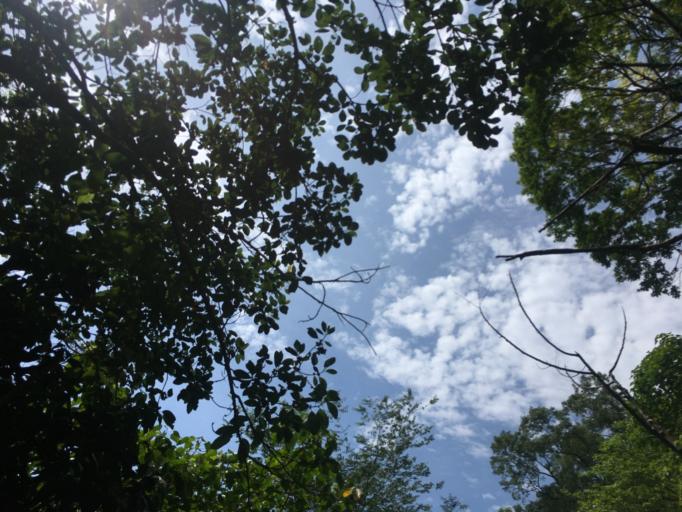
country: TW
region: Taiwan
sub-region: Hualien
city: Hualian
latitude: 24.0200
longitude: 121.5749
